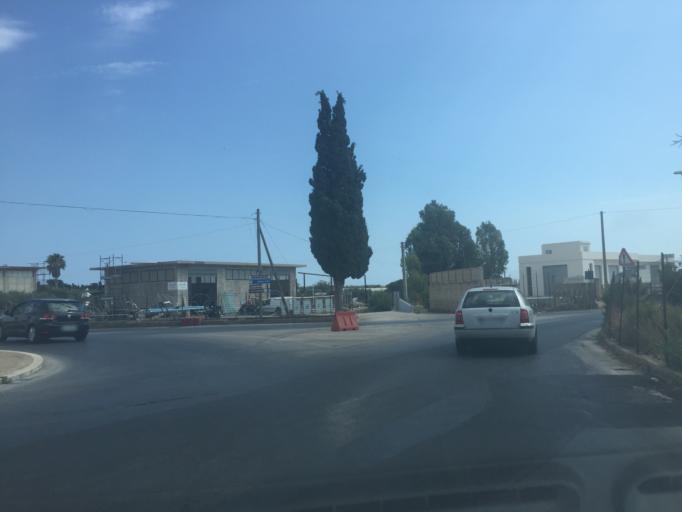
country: IT
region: Sicily
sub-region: Ragusa
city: Santa Croce Camerina
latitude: 36.8217
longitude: 14.5197
